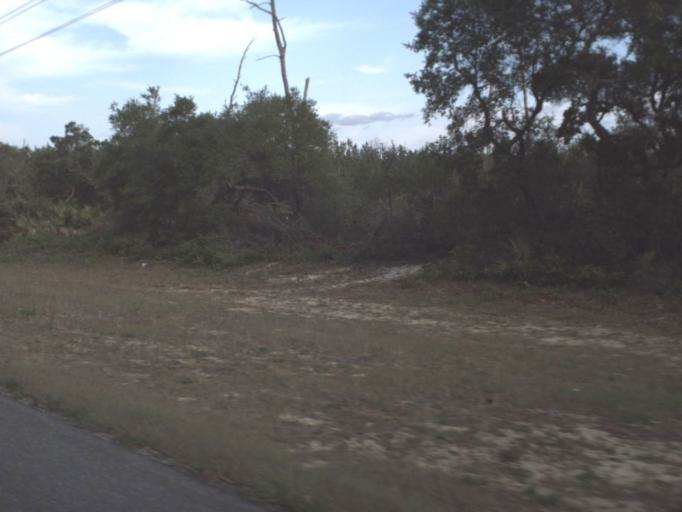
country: US
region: Florida
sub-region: Lake County
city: Astor
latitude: 29.1778
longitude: -81.7415
